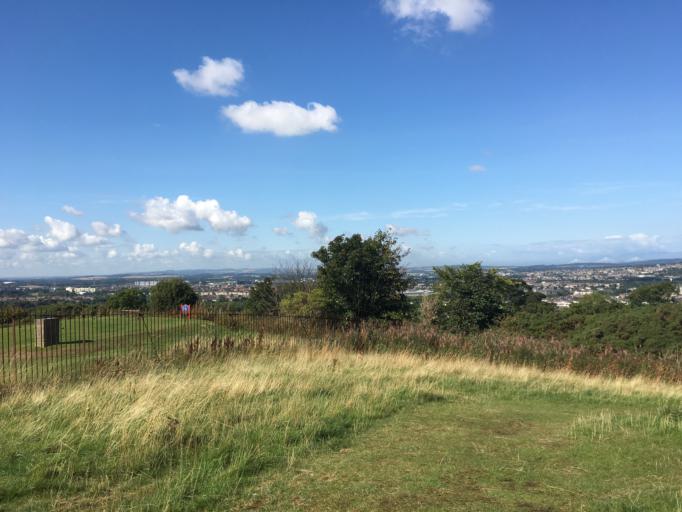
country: GB
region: Scotland
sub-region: Edinburgh
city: Colinton
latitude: 55.9212
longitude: -3.2316
